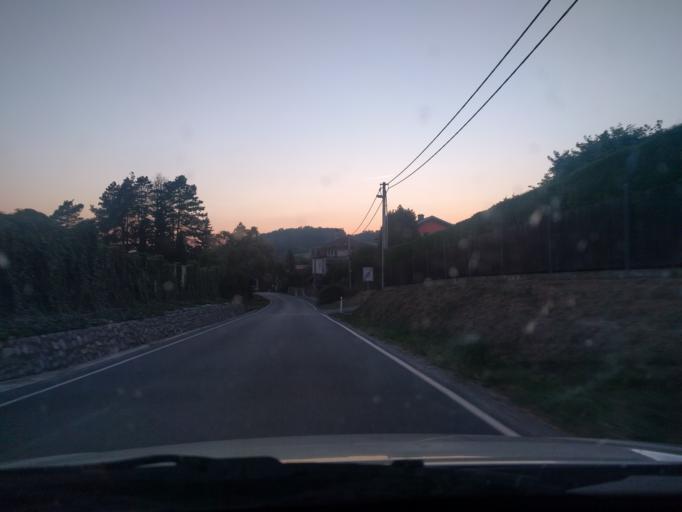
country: CZ
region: Central Bohemia
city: Tynec nad Sazavou
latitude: 49.8561
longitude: 14.5630
